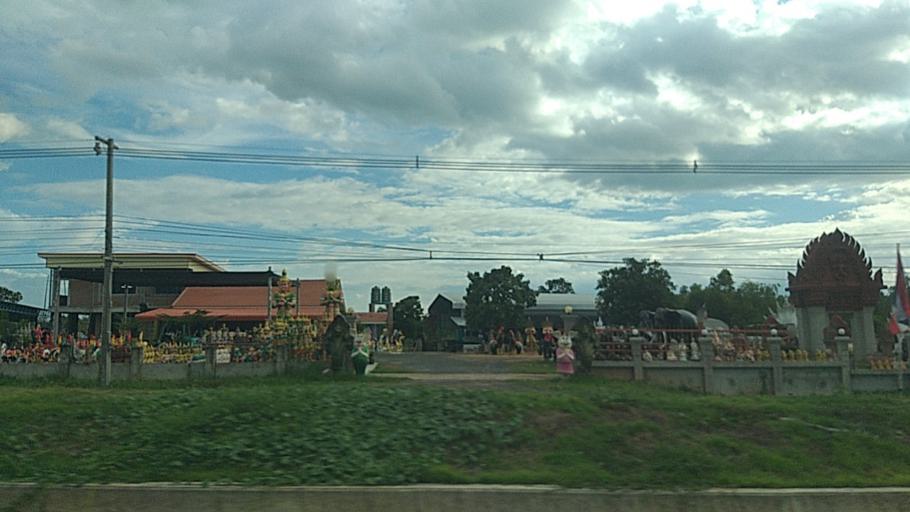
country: TH
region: Surin
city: Kap Choeng
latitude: 14.5549
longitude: 103.5049
